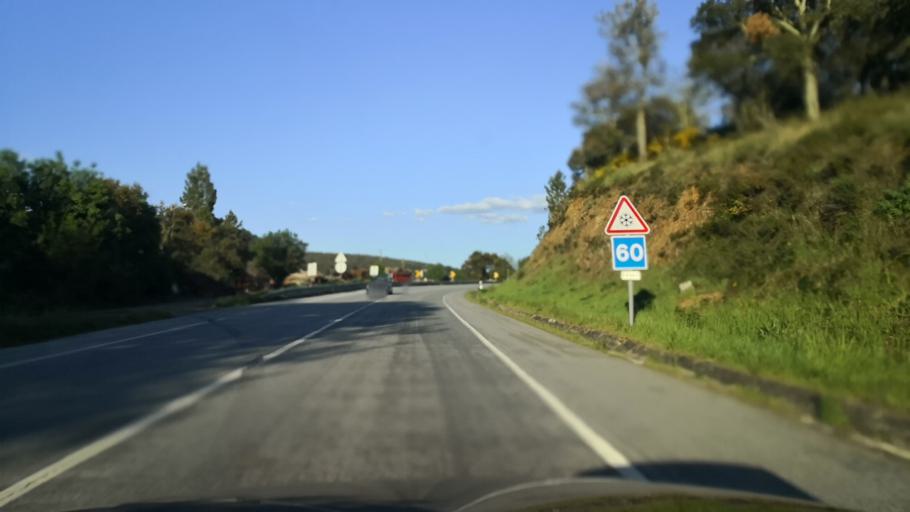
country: PT
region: Portalegre
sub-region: Marvao
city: Marvao
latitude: 39.3818
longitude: -7.3808
